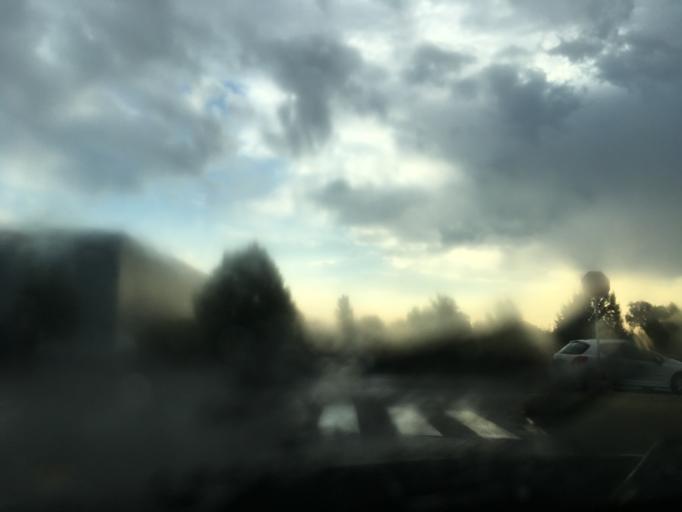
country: FR
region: Midi-Pyrenees
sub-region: Departement de la Haute-Garonne
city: Tournefeuille
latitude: 43.5654
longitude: 1.3367
